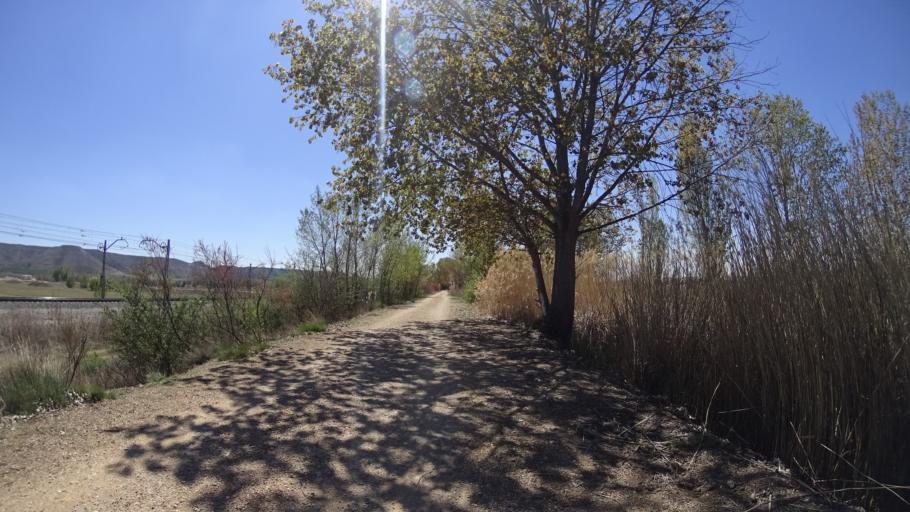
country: ES
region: Castille and Leon
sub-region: Provincia de Valladolid
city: Cabezon
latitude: 41.7702
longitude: -4.6202
